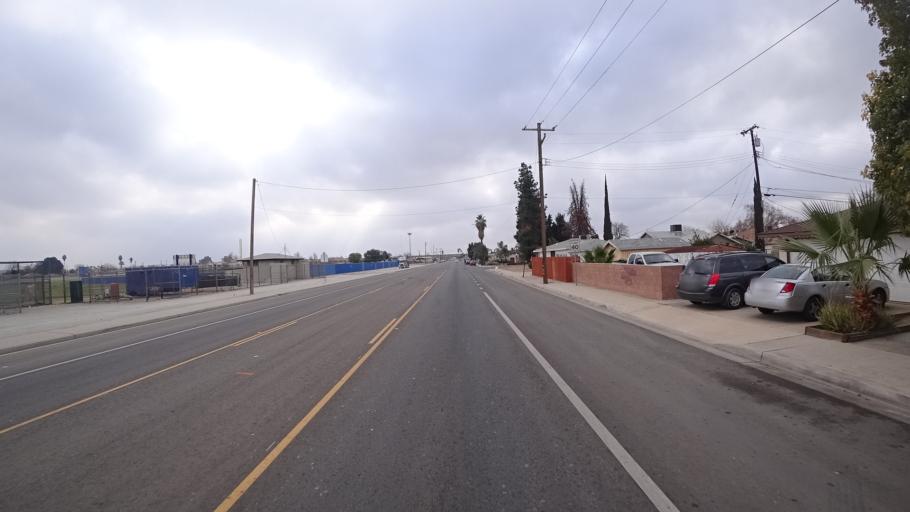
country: US
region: California
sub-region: Kern County
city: Bakersfield
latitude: 35.3577
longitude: -119.0119
